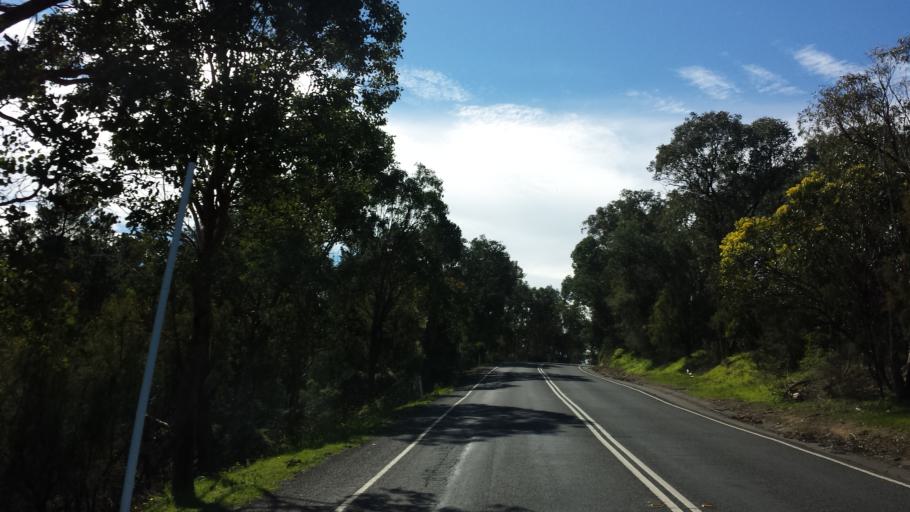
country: AU
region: Victoria
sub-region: Nillumbik
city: North Warrandyte
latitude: -37.7116
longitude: 145.2215
